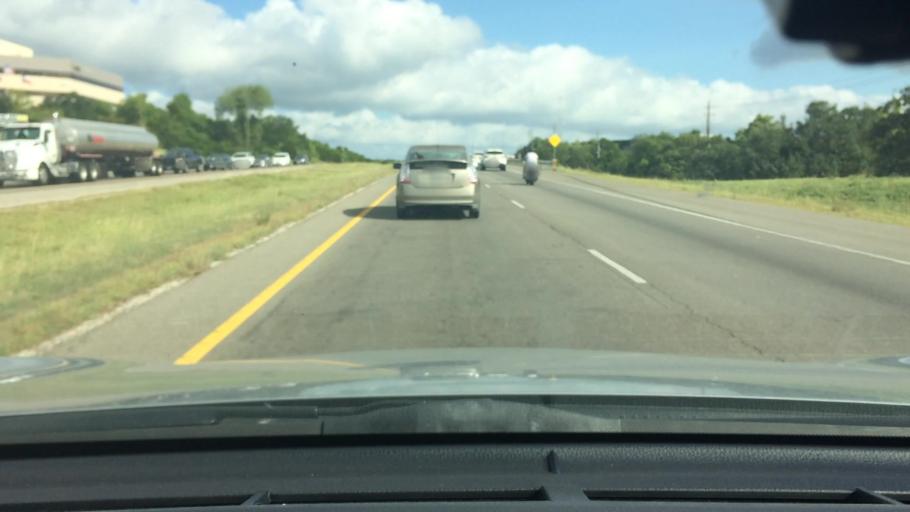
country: US
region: Texas
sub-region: Travis County
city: Lost Creek
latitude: 30.2850
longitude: -97.8249
